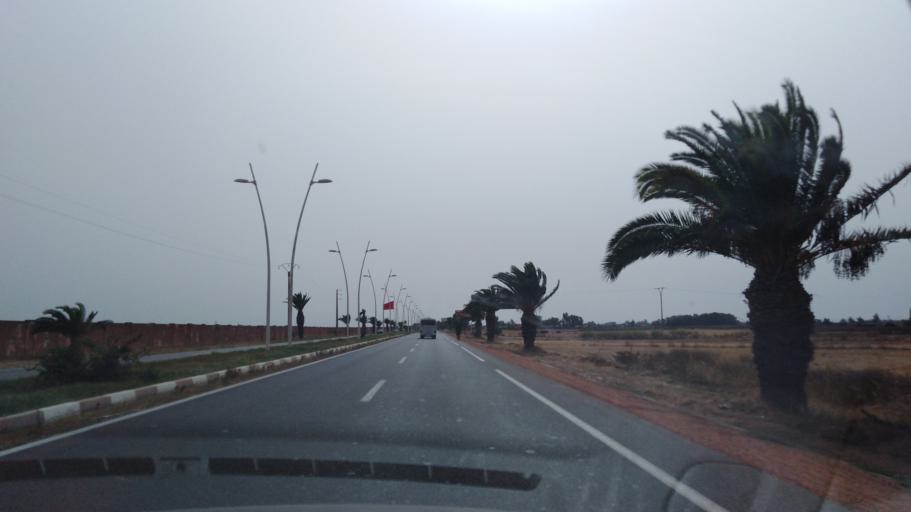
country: MA
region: Chaouia-Ouardigha
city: Nouaseur
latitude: 33.3956
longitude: -7.5913
